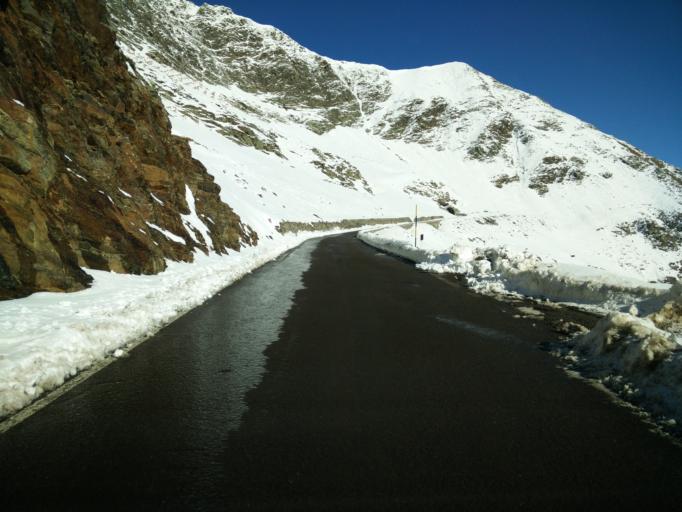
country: IT
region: Trentino-Alto Adige
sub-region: Bolzano
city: Moso in Passiria
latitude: 46.8873
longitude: 11.1101
